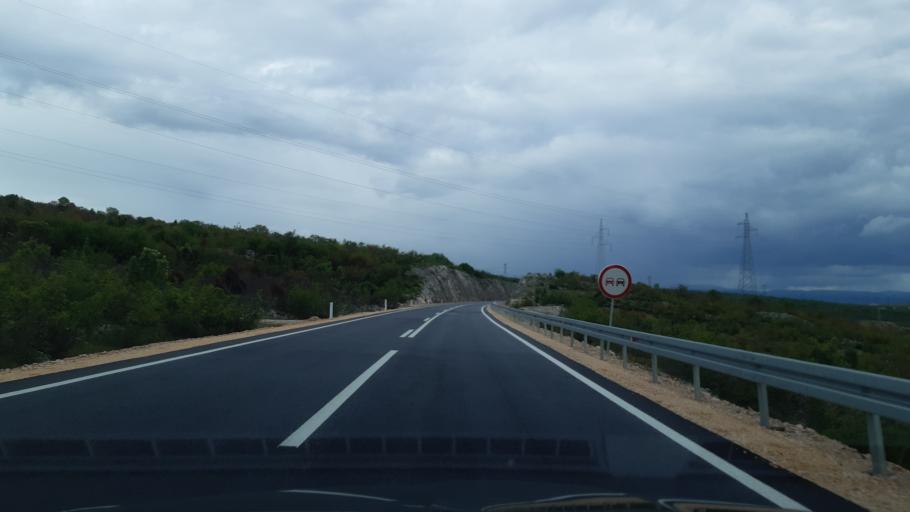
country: BA
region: Federation of Bosnia and Herzegovina
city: Ilici
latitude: 43.3238
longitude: 17.7457
